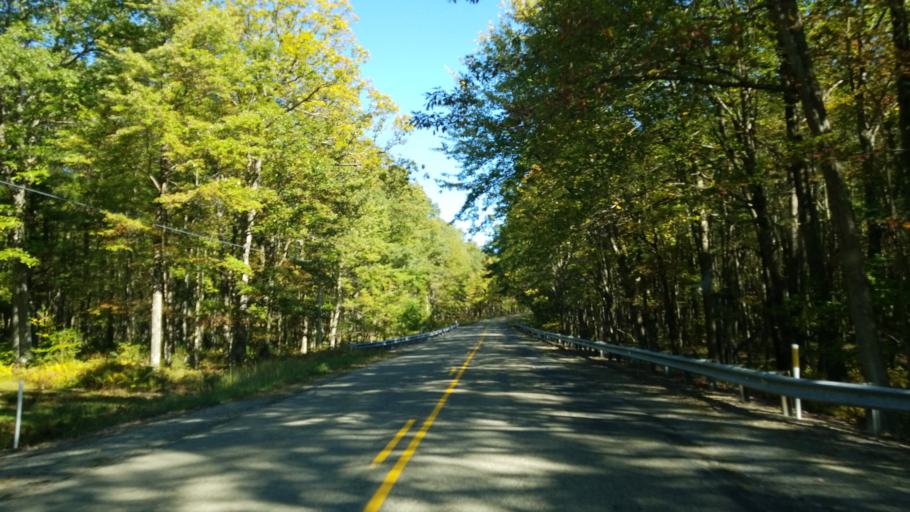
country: US
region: Pennsylvania
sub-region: Clearfield County
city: Shiloh
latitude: 41.2543
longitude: -78.3618
